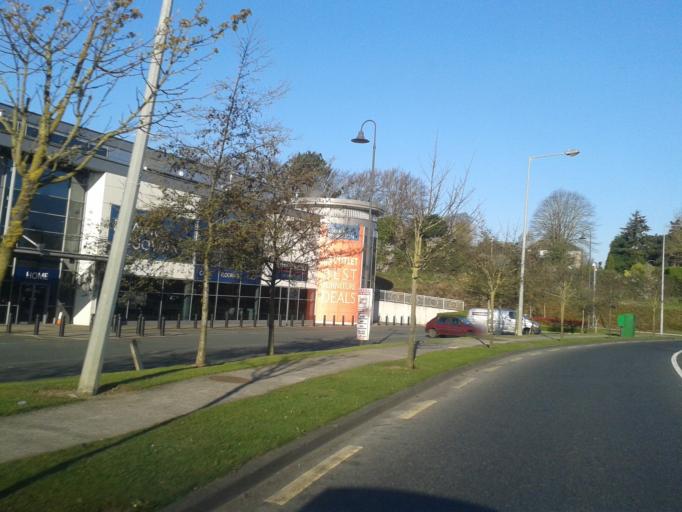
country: IE
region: Leinster
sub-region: Fingal County
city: Swords
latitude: 53.4485
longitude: -6.2228
